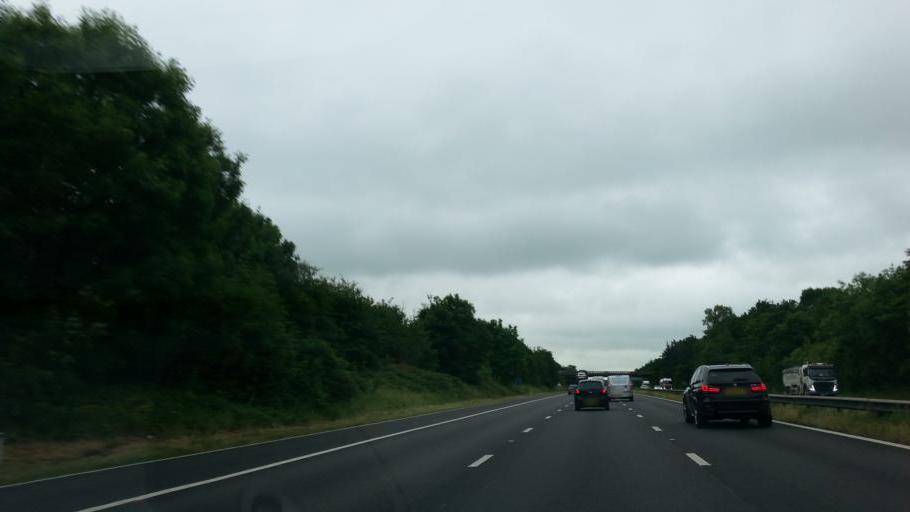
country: GB
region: England
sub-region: Leicestershire
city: Cosby
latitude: 52.5390
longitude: -1.1815
